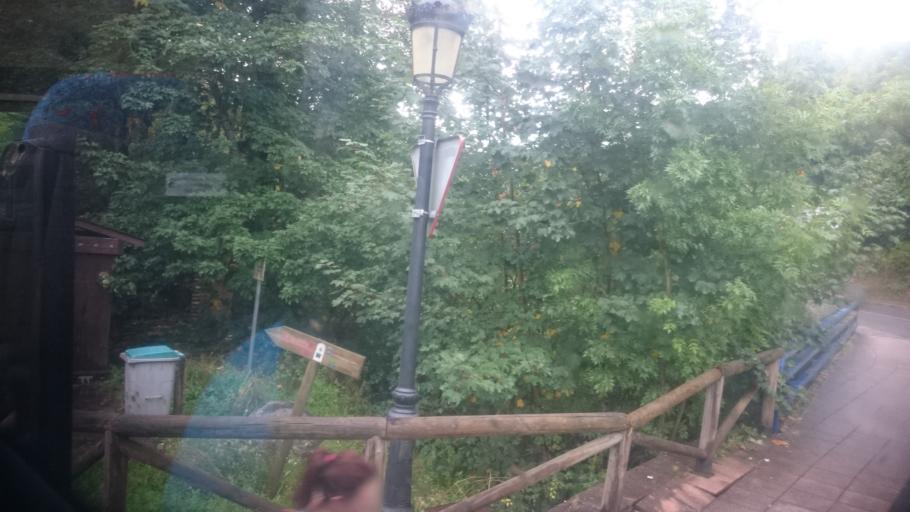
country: ES
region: Asturias
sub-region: Province of Asturias
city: Amieva
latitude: 43.3126
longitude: -5.0600
